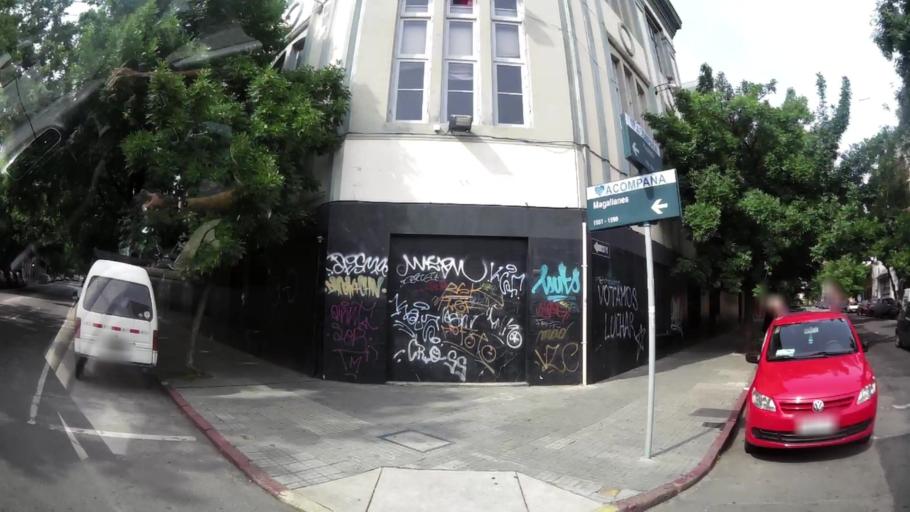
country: UY
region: Montevideo
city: Montevideo
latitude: -34.9003
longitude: -56.1814
